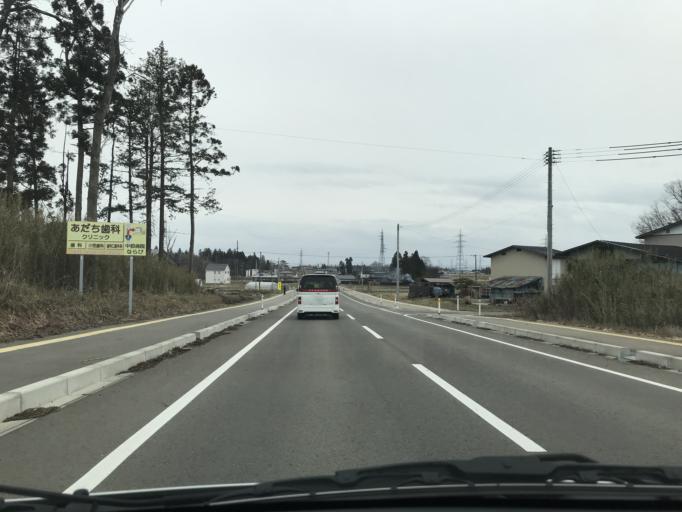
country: JP
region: Iwate
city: Hanamaki
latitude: 39.3494
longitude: 141.1027
